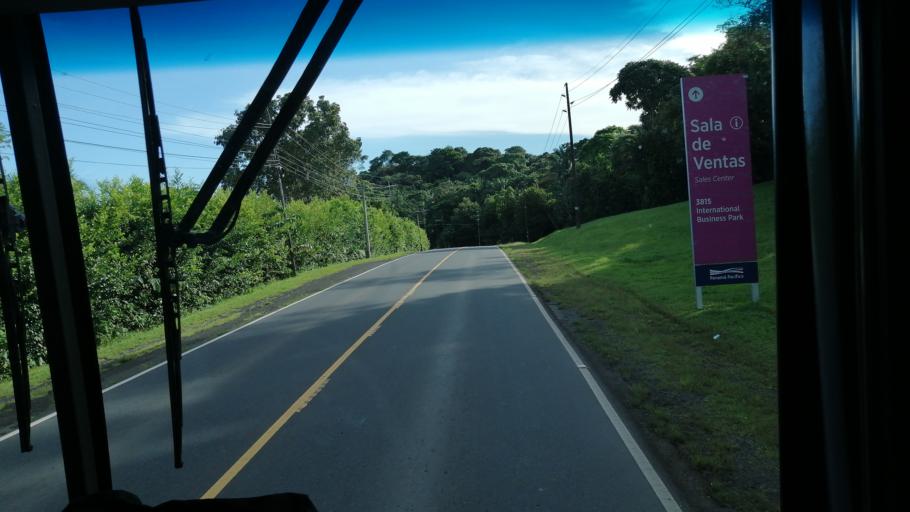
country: PA
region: Panama
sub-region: Distrito de Panama
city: Ancon
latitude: 8.9474
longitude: -79.5909
